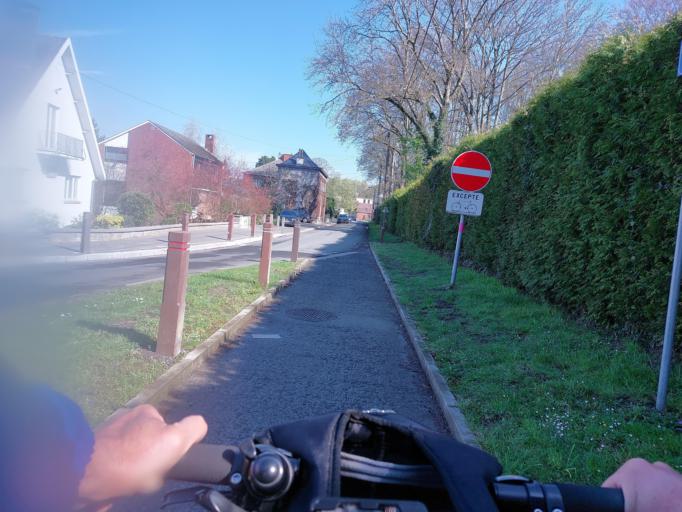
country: BE
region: Wallonia
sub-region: Province du Hainaut
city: Mons
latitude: 50.4507
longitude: 3.9723
